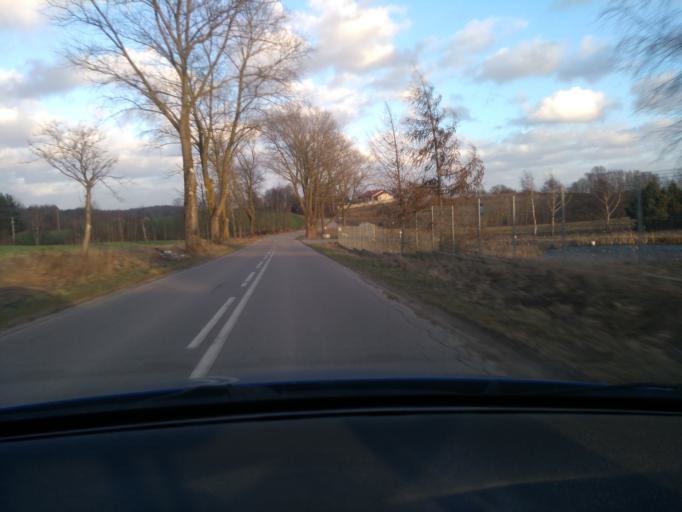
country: PL
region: Pomeranian Voivodeship
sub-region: Powiat kartuski
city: Przodkowo
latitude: 54.4162
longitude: 18.3006
